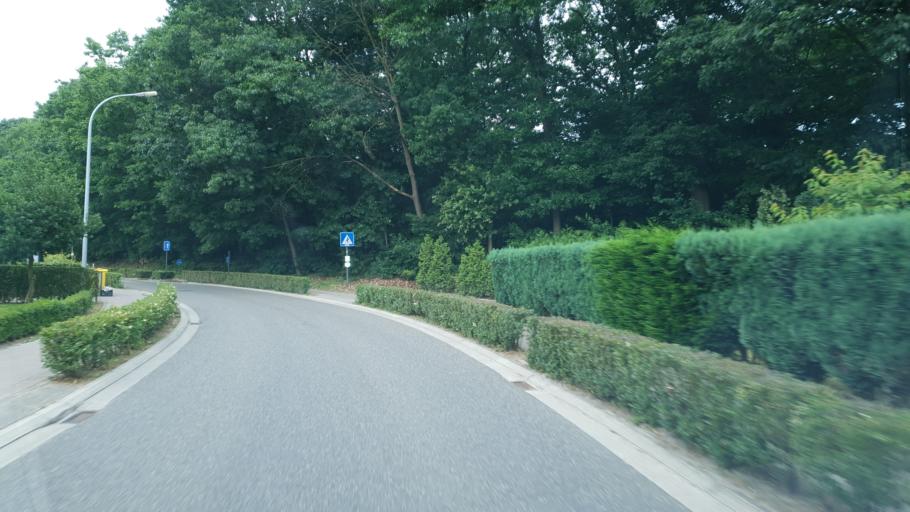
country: BE
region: Flanders
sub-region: Provincie Antwerpen
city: Merksplas
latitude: 51.3607
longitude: 4.8419
